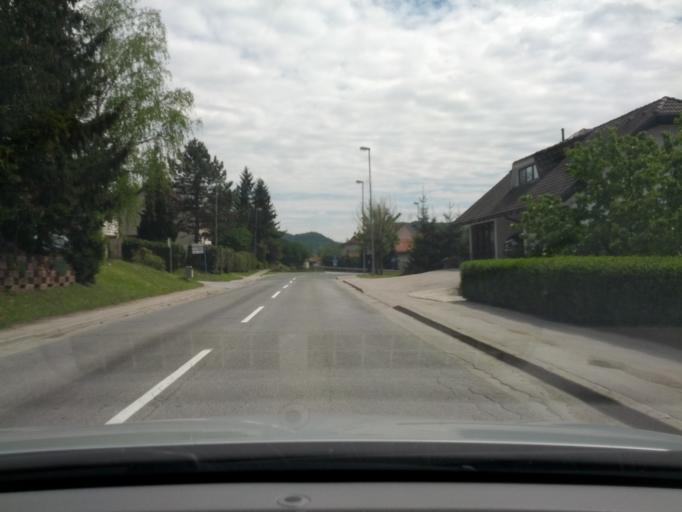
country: SI
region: Sentjur pri Celju
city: Sentjur
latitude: 46.2154
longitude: 15.3984
